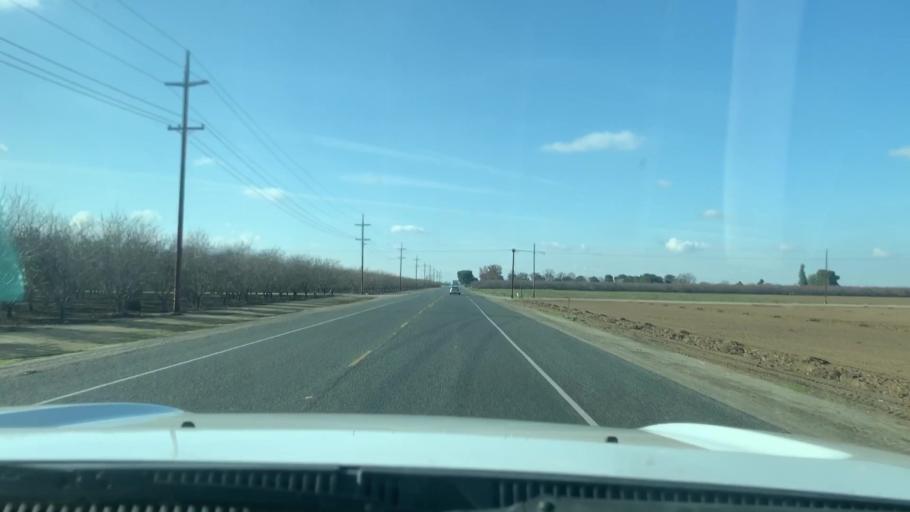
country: US
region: California
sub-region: Kern County
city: Wasco
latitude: 35.6015
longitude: -119.3745
